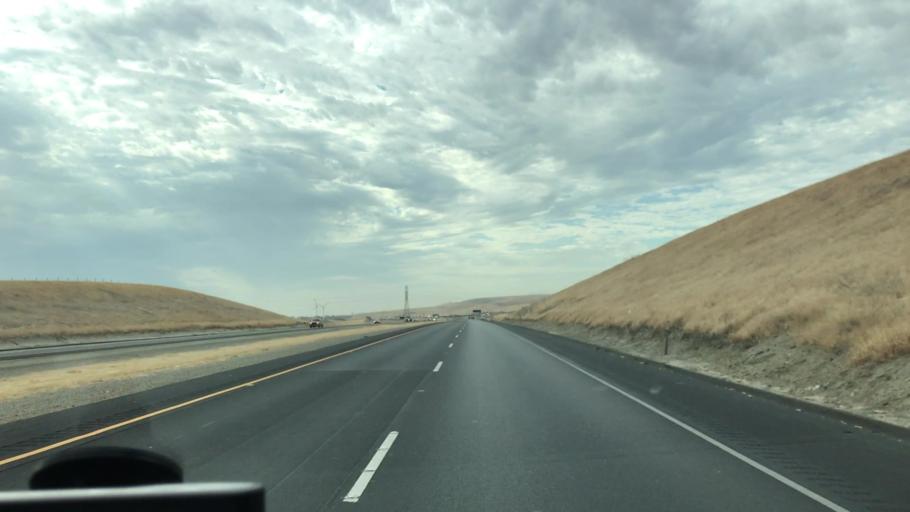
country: US
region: California
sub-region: San Joaquin County
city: Mountain House
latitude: 37.7315
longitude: -121.5489
